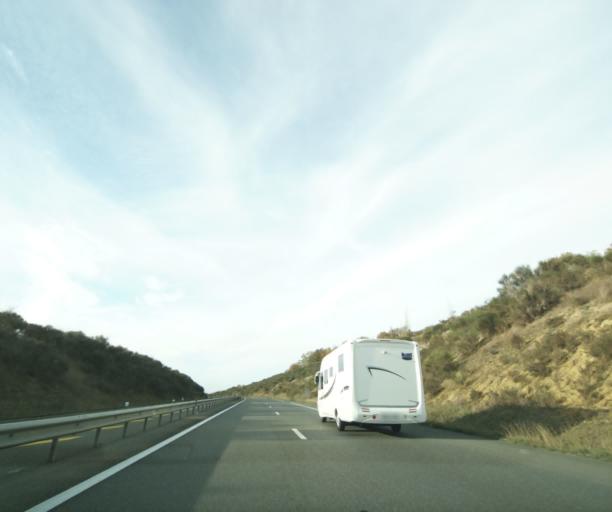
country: FR
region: Midi-Pyrenees
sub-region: Departement du Gers
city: Aubiet
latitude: 43.6392
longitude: 0.8197
